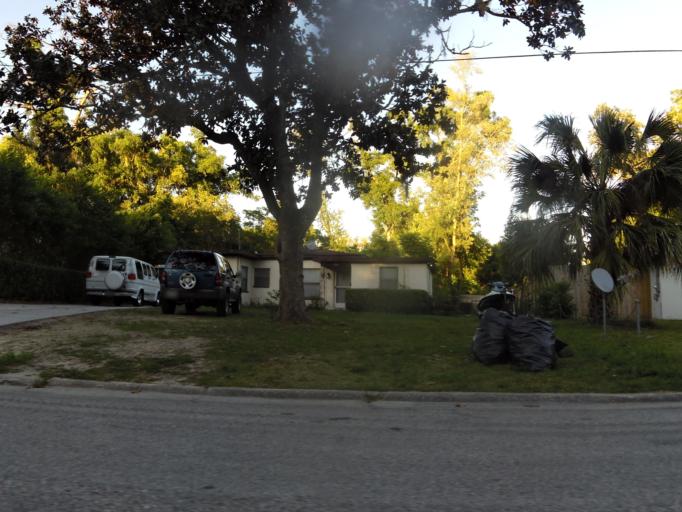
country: US
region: Florida
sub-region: Duval County
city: Jacksonville
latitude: 30.2644
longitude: -81.6387
